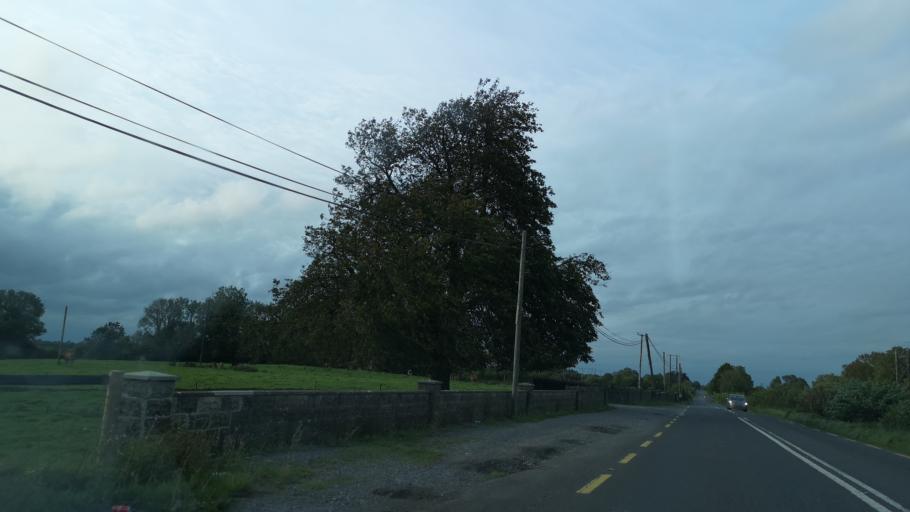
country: IE
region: Leinster
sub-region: Uibh Fhaili
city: Ferbane
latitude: 53.3162
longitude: -7.8212
